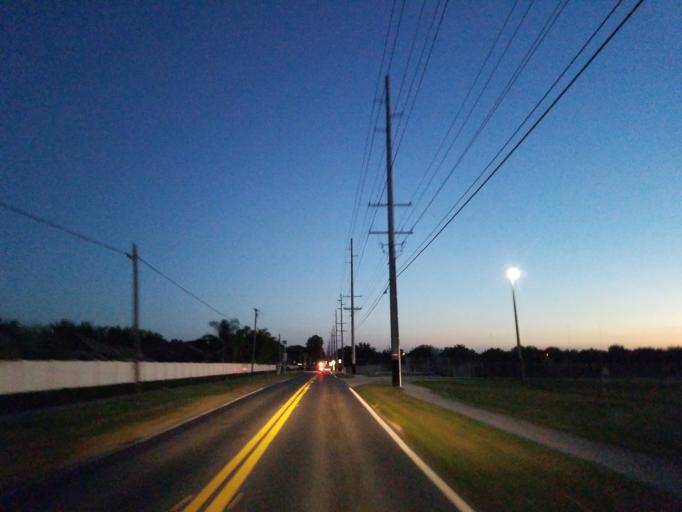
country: US
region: Florida
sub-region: Hillsborough County
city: Bloomingdale
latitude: 27.9070
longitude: -82.2277
